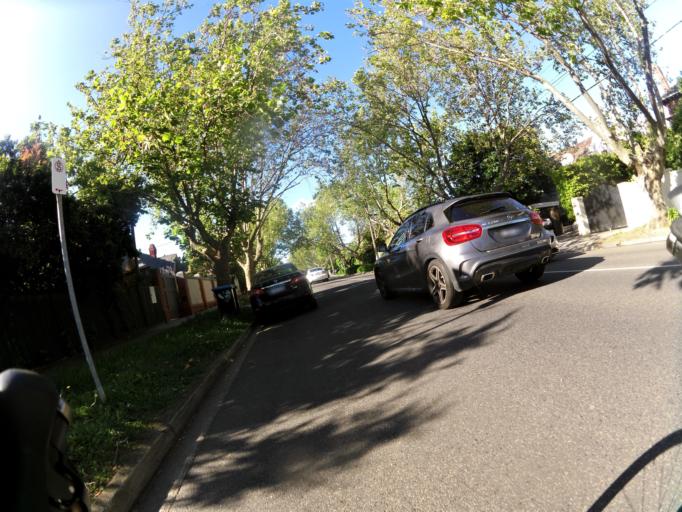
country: AU
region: Victoria
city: Toorak
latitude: -37.8543
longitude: 145.0208
